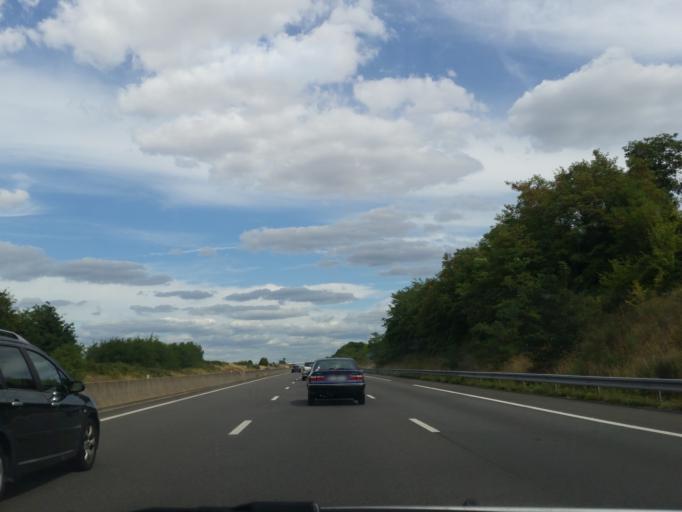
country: FR
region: Centre
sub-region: Departement du Loir-et-Cher
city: Saint-Sulpice-de-Pommeray
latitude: 47.6176
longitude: 1.2703
